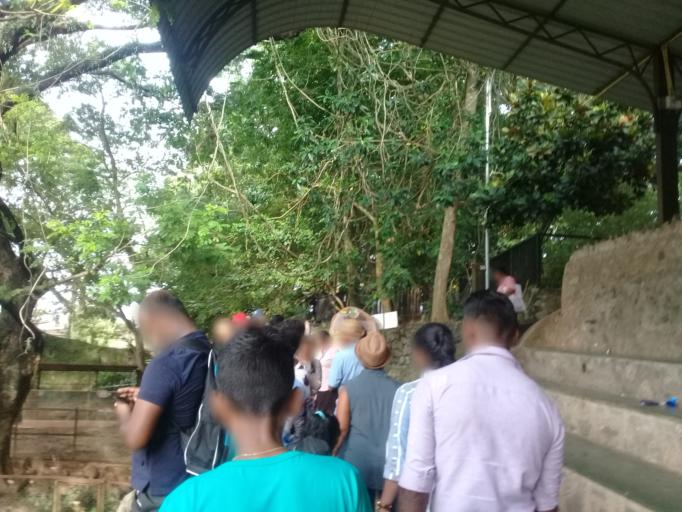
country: LK
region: Western
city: Galkissa
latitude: 6.8578
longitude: 79.8747
